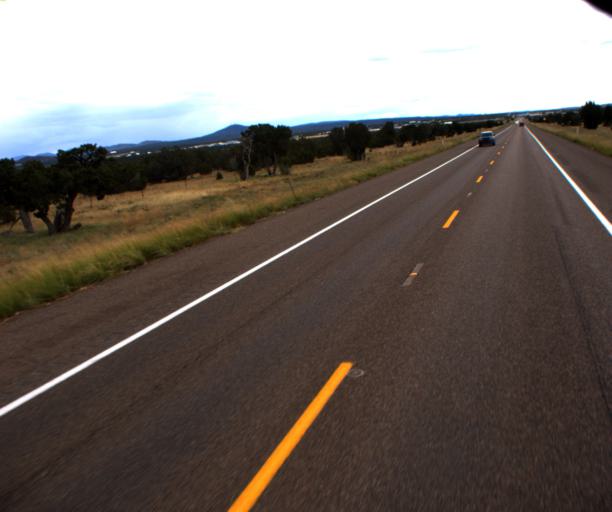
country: US
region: Arizona
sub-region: Navajo County
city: Show Low
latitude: 34.2789
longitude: -110.0266
